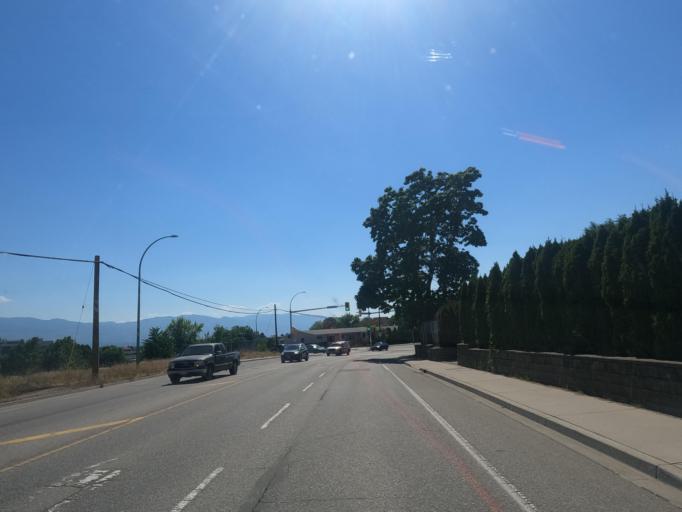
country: CA
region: British Columbia
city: Kelowna
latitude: 49.8869
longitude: -119.4615
